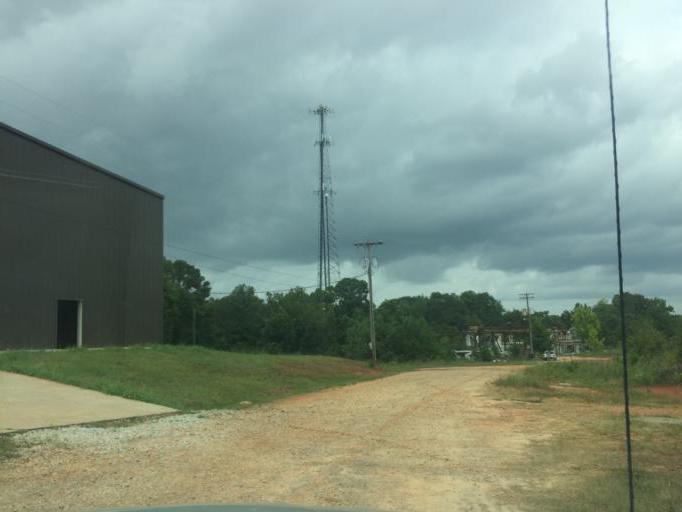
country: US
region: Georgia
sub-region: Elbert County
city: Elberton
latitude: 34.1295
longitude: -82.8629
